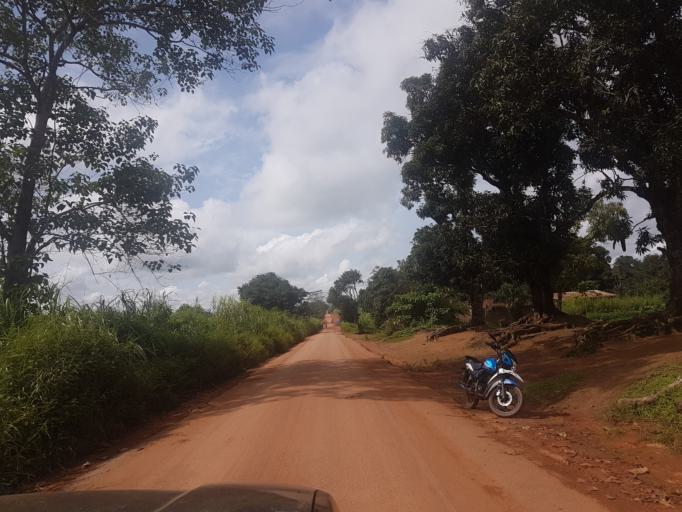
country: GN
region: Nzerekore
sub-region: Prefecture de Guekedou
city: Gueckedou
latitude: 8.6717
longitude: -10.1207
